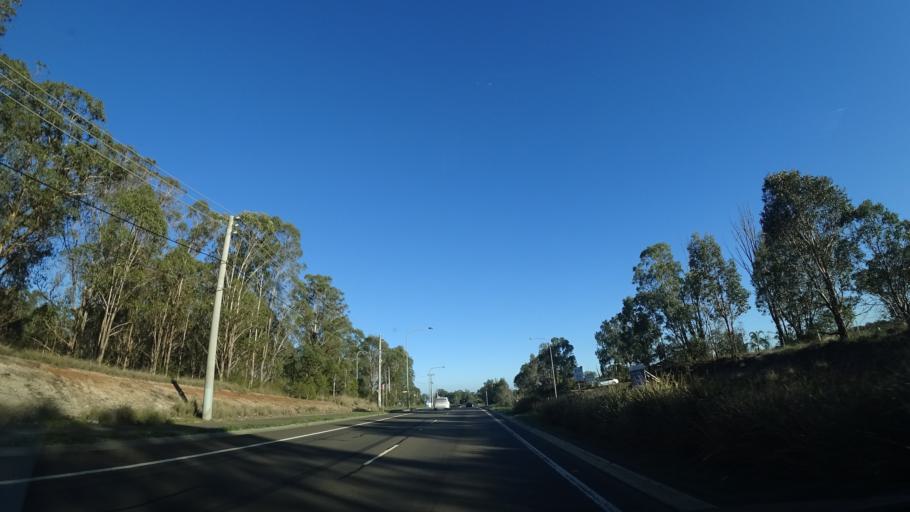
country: AU
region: New South Wales
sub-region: Blacktown
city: Riverstone
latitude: -33.6516
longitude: 150.8652
